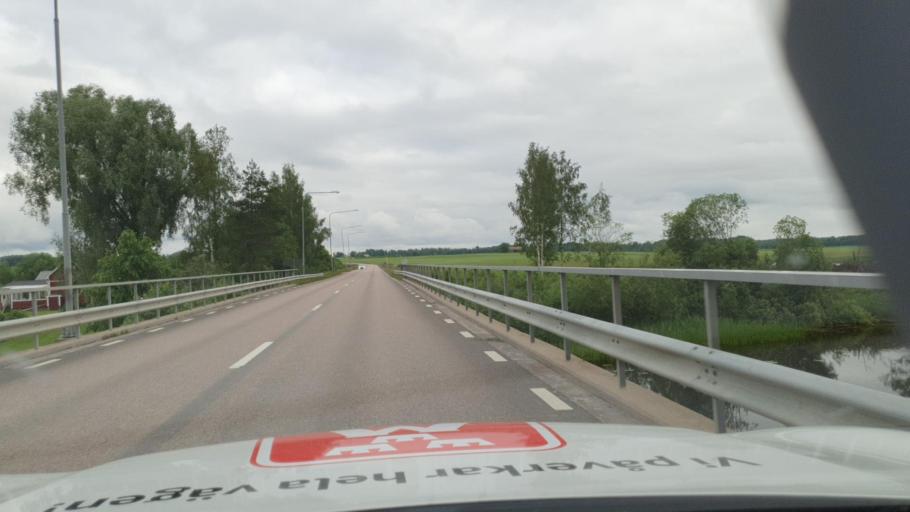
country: SE
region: Vaermland
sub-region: Kils Kommun
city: Kil
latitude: 59.5427
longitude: 13.2972
